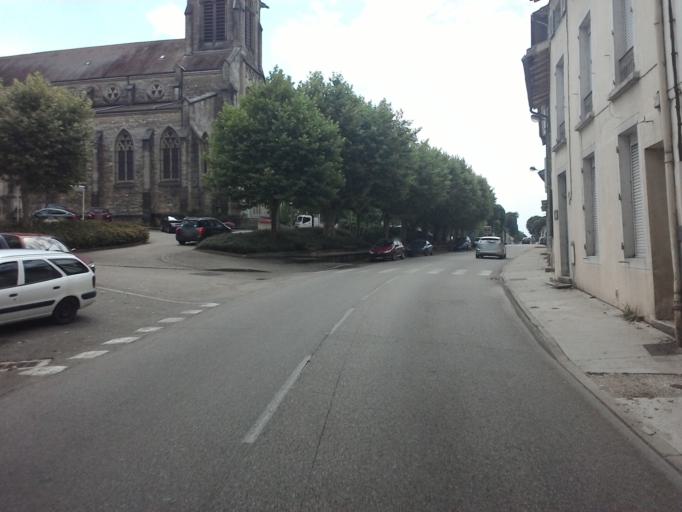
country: FR
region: Rhone-Alpes
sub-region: Departement de l'Ain
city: Coligny
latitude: 46.3844
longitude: 5.3459
